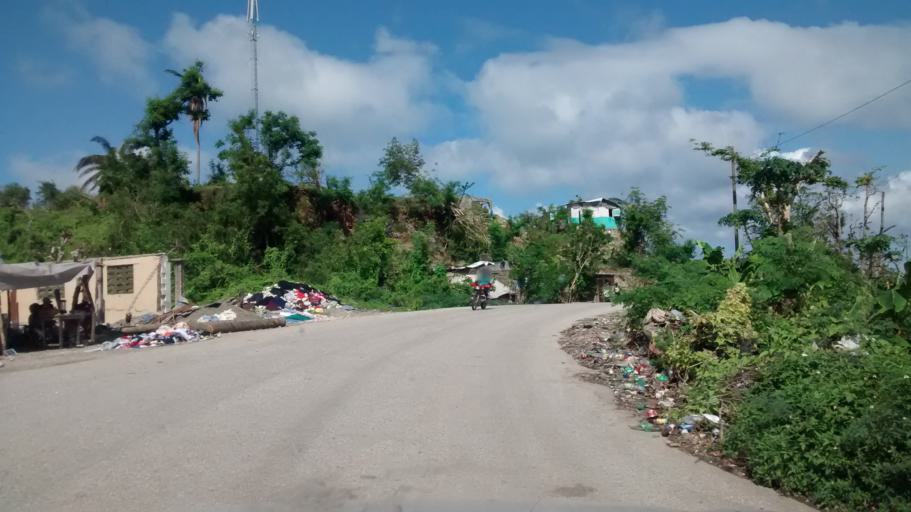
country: HT
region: Grandans
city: Jeremie
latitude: 18.6122
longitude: -74.0834
